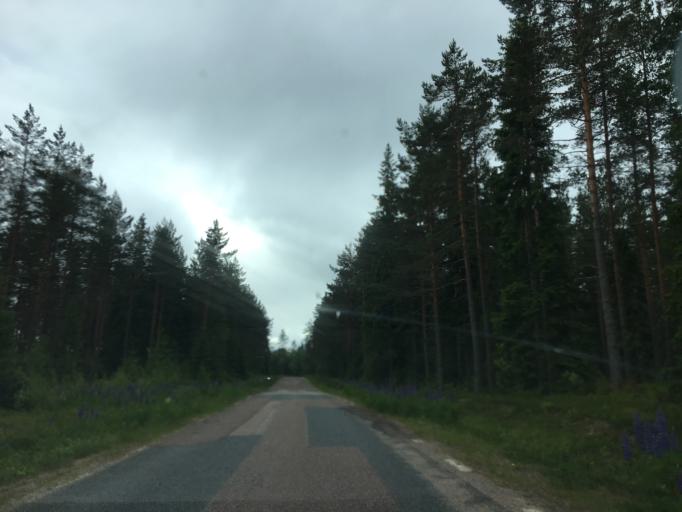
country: SE
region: OErebro
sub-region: Hallefors Kommun
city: Haellefors
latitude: 60.0602
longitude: 14.4936
